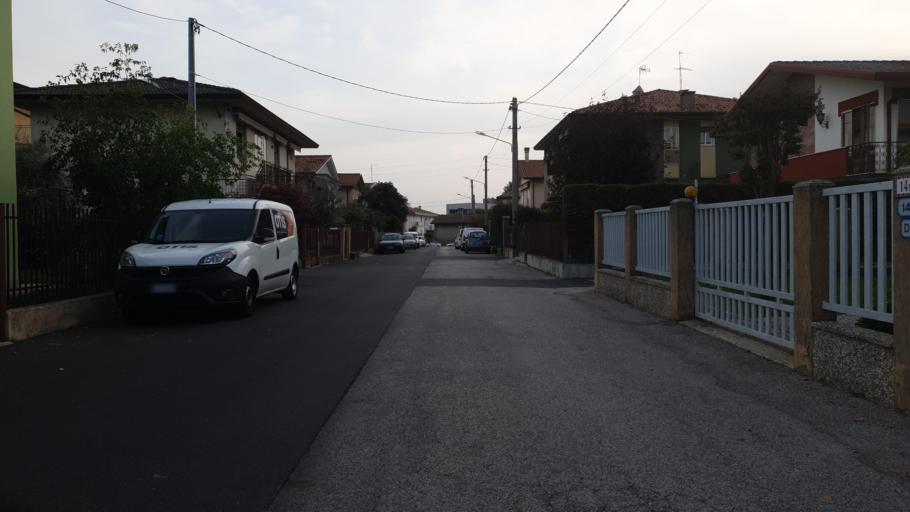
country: IT
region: Veneto
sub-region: Provincia di Padova
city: Noventa
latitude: 45.3997
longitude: 11.9401
